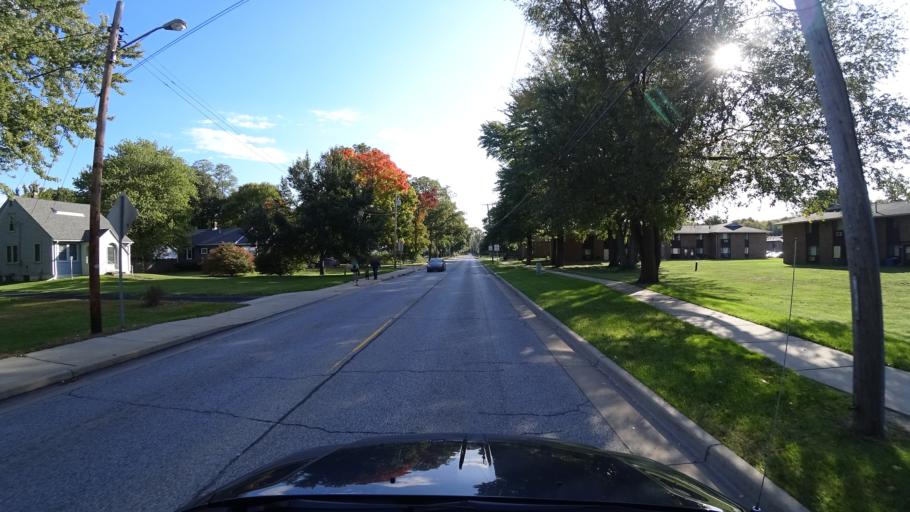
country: US
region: Indiana
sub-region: LaPorte County
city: Trail Creek
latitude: 41.6947
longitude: -86.8691
